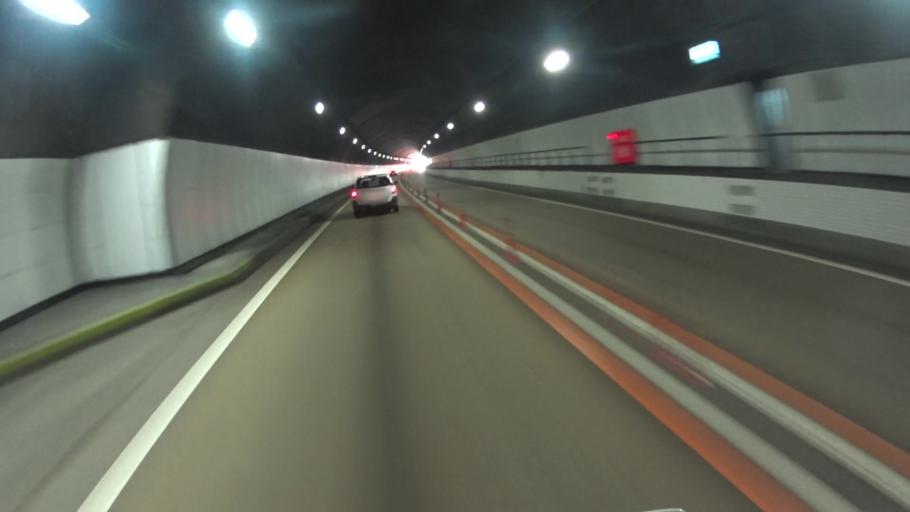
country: JP
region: Kyoto
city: Kameoka
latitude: 35.1395
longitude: 135.4487
